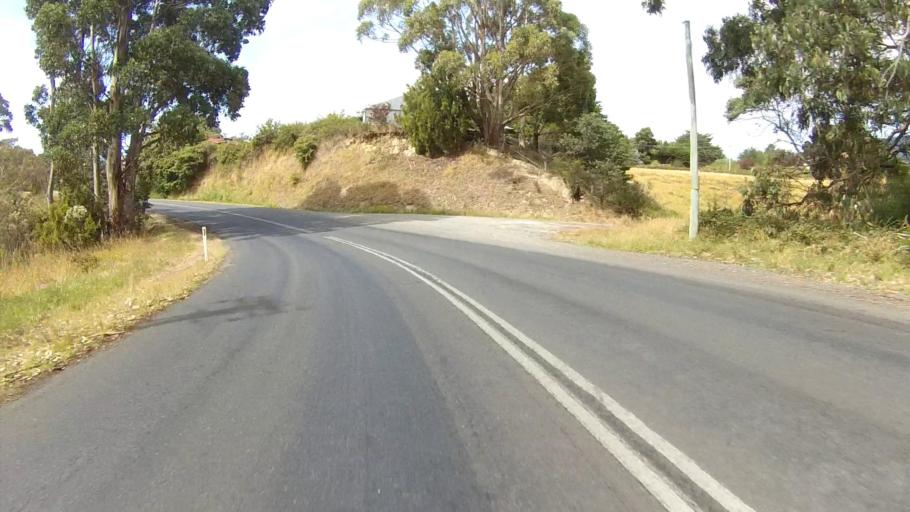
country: AU
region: Tasmania
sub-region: Kingborough
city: Kettering
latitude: -43.1477
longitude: 147.2391
